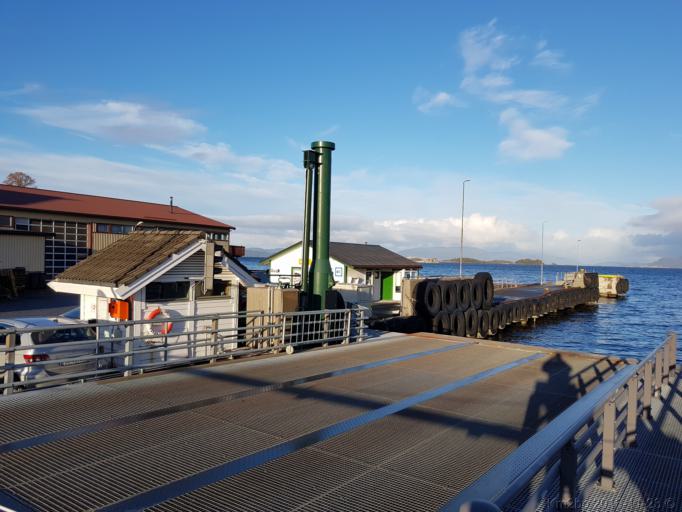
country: NO
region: Hordaland
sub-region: Tysnes
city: Uggdal
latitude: 60.0467
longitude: 5.5242
